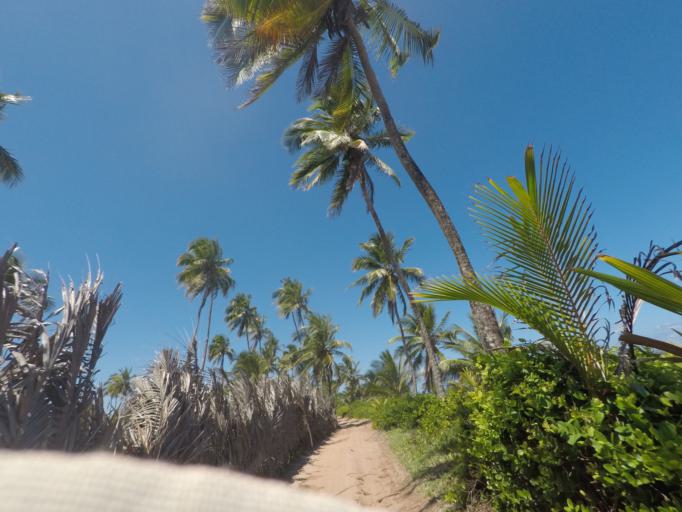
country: BR
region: Bahia
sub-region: Marau
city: Marau
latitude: -13.9951
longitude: -38.9434
